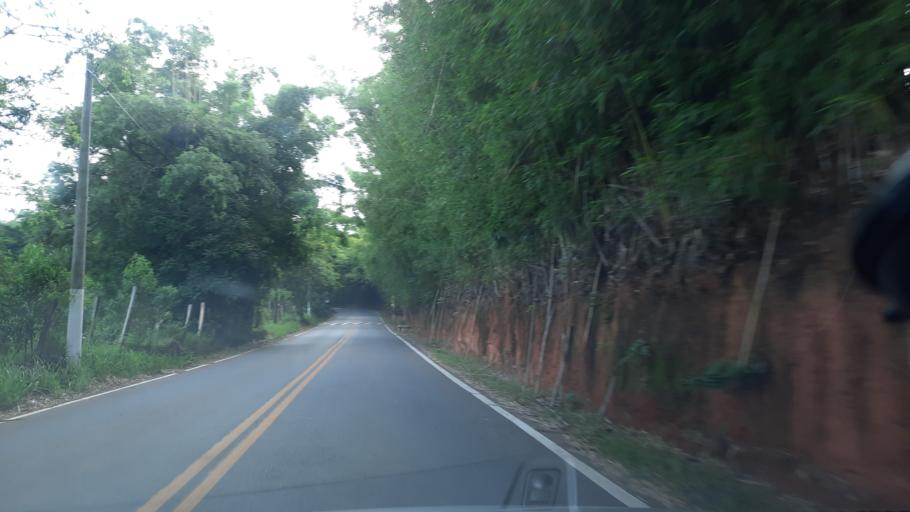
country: BR
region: Sao Paulo
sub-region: Atibaia
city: Atibaia
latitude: -23.0955
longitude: -46.5149
